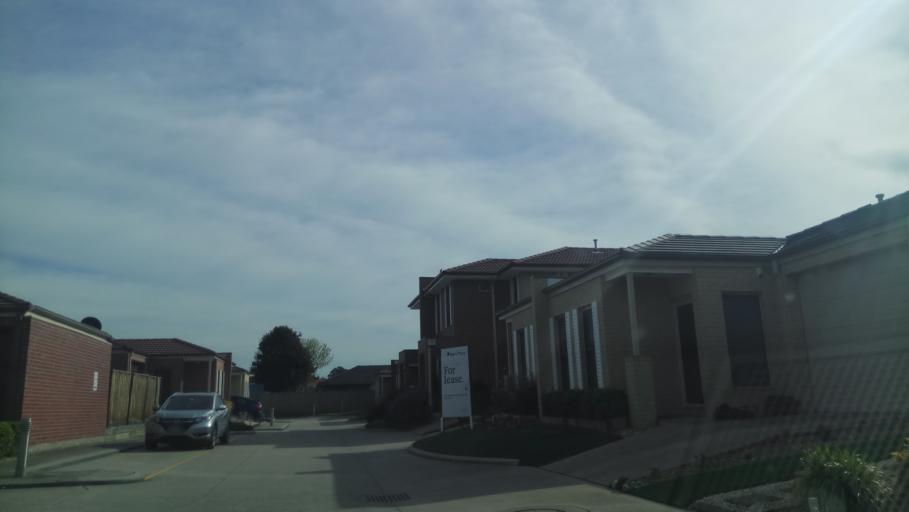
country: AU
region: Victoria
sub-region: Kingston
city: Waterways
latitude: -38.0026
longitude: 145.1448
